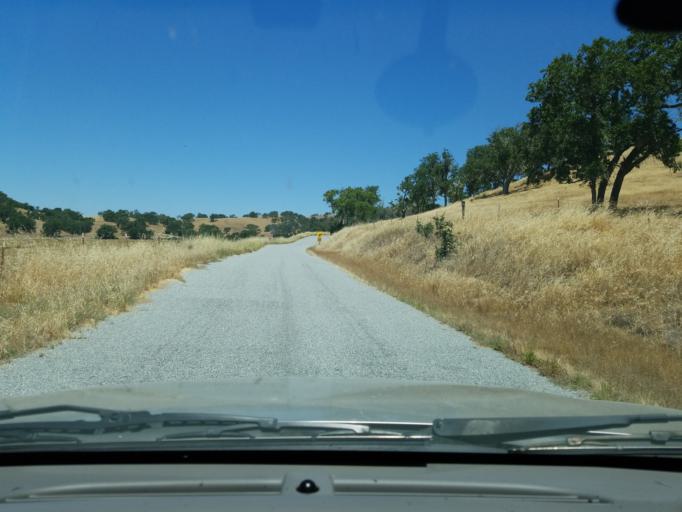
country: US
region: California
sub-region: Monterey County
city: Gonzales
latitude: 36.3969
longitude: -121.5760
